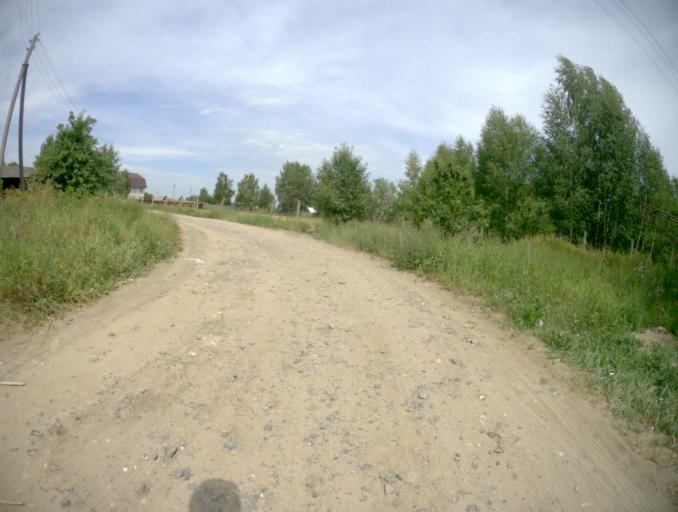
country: RU
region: Vladimir
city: Raduzhnyy
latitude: 56.0255
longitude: 40.3179
